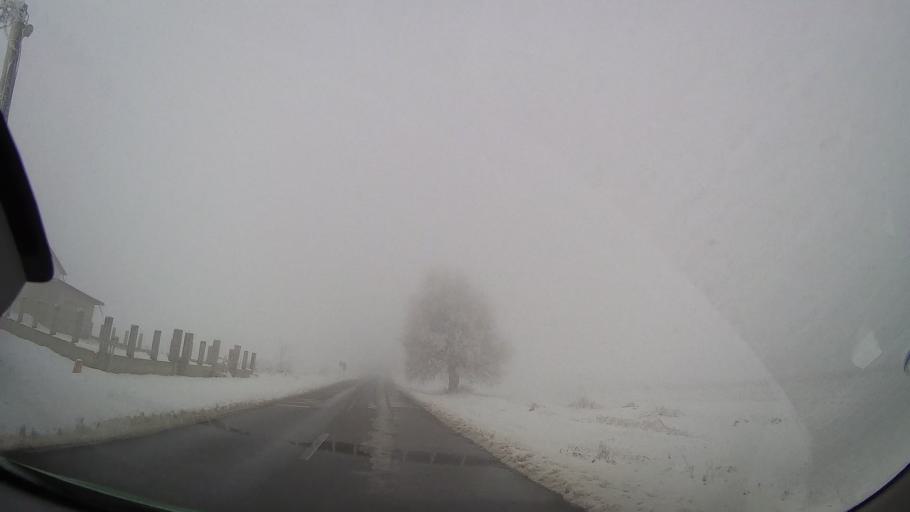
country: RO
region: Neamt
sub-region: Comuna Sabaoani
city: Sabaoani
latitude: 47.0307
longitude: 26.8578
